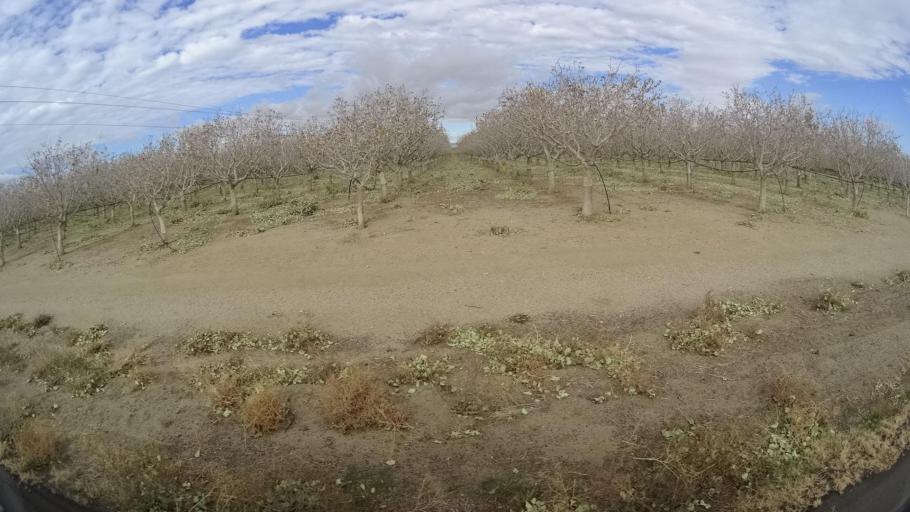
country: US
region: California
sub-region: Kern County
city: Rosamond
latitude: 34.8199
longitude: -118.3182
